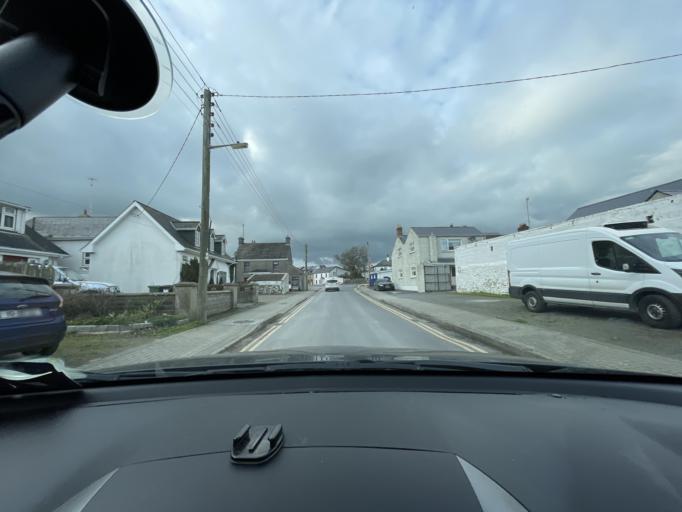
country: IE
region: Leinster
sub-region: Lu
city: Clogherhead
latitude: 53.7908
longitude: -6.2378
